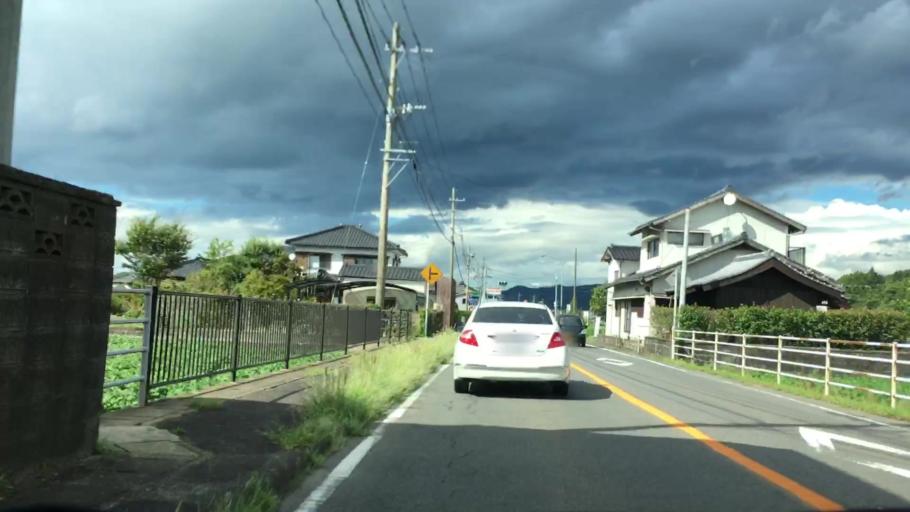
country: JP
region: Saga Prefecture
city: Imaricho-ko
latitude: 33.2506
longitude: 129.8529
